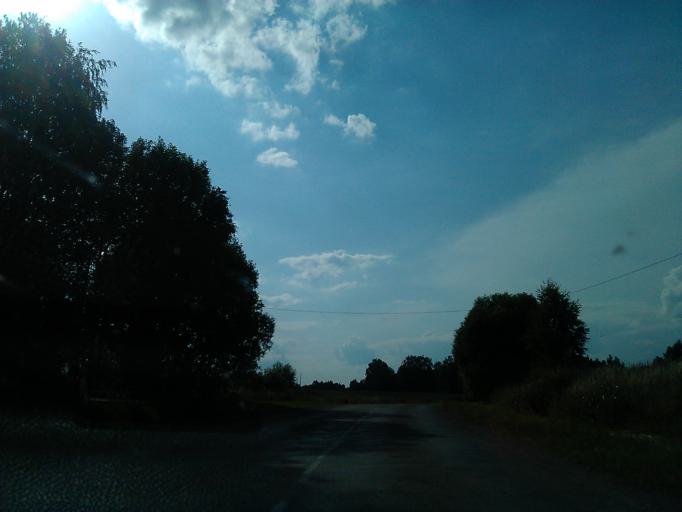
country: LV
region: Skrunda
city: Skrunda
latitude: 56.6835
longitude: 21.8972
